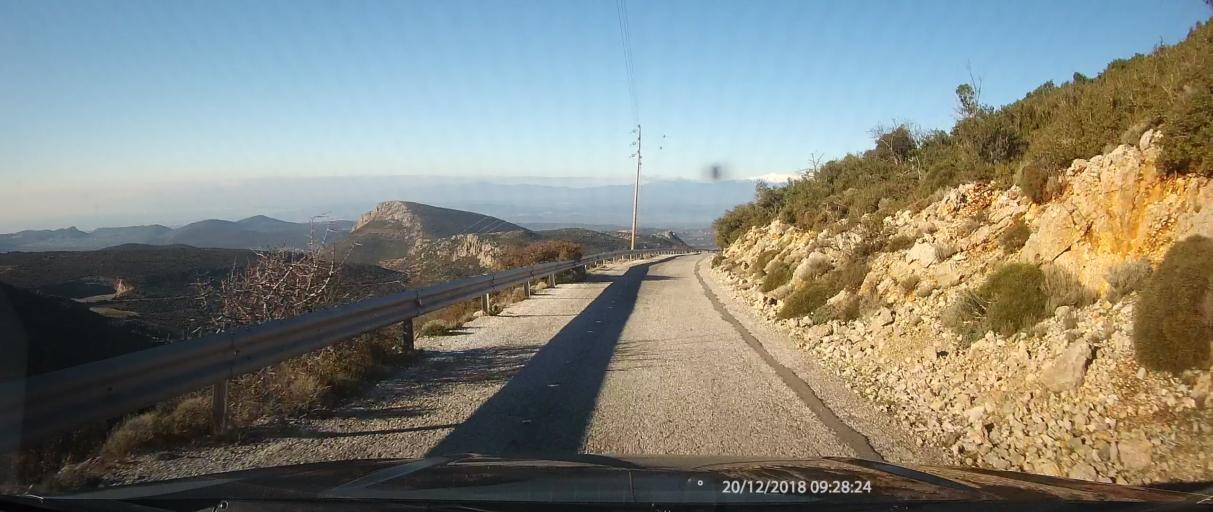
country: GR
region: Peloponnese
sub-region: Nomos Lakonias
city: Kato Glikovrisi
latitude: 36.9602
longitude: 22.8543
